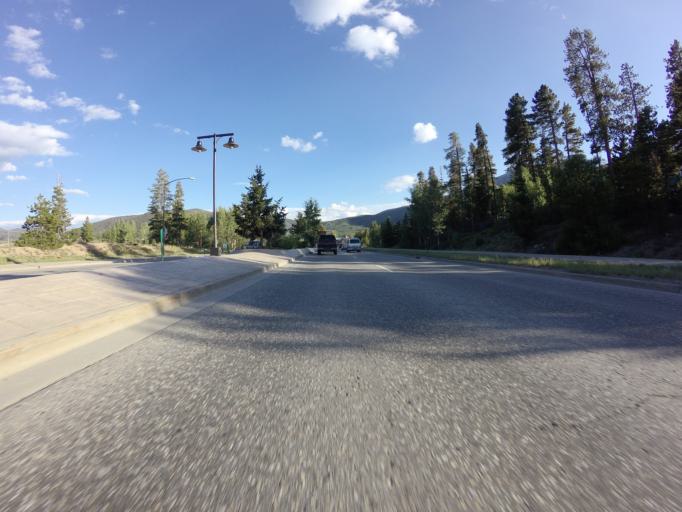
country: US
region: Colorado
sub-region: Summit County
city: Frisco
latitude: 39.5809
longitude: -106.0934
